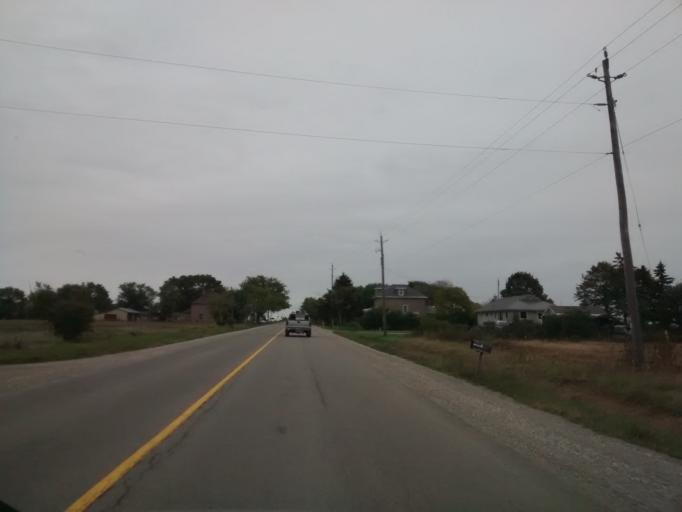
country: CA
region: Ontario
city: Hamilton
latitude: 42.8736
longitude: -79.7211
